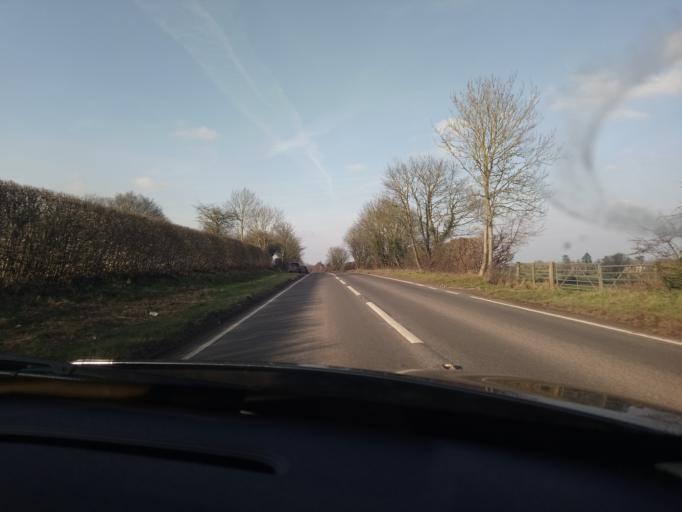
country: GB
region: England
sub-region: Shropshire
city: Clive
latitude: 52.7869
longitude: -2.7560
